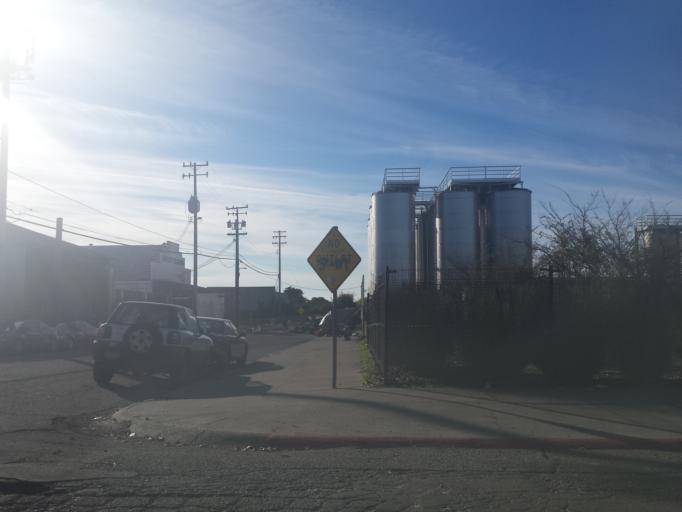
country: US
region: California
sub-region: Alameda County
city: Albany
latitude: 37.8649
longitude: -122.2990
